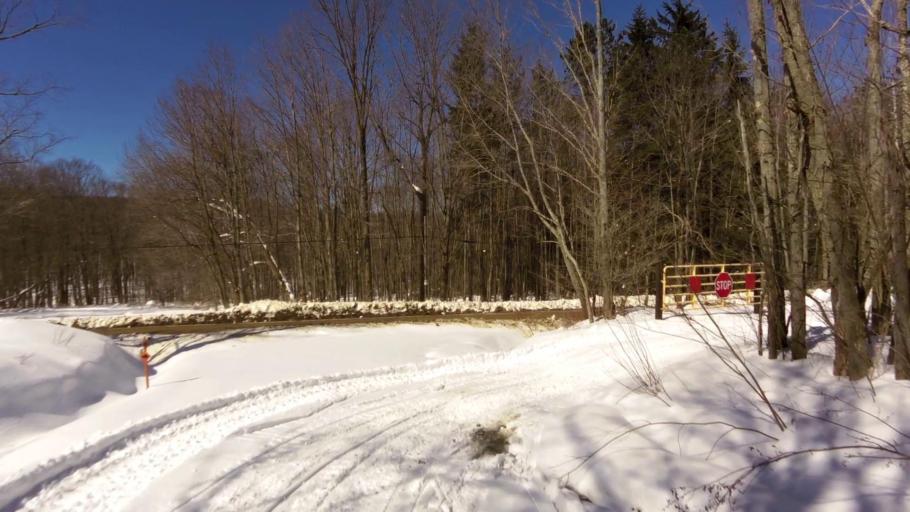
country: US
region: New York
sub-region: Allegany County
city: Cuba
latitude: 42.3268
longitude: -78.2498
